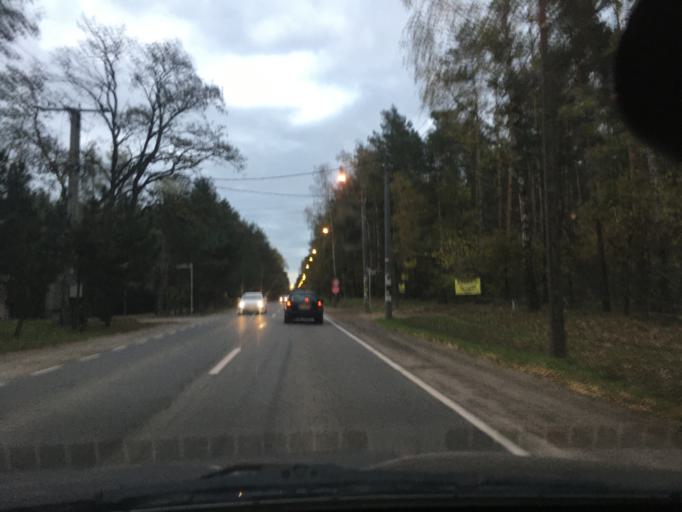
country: PL
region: Masovian Voivodeship
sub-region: Powiat piaseczynski
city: Lesznowola
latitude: 52.1004
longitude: 20.8933
